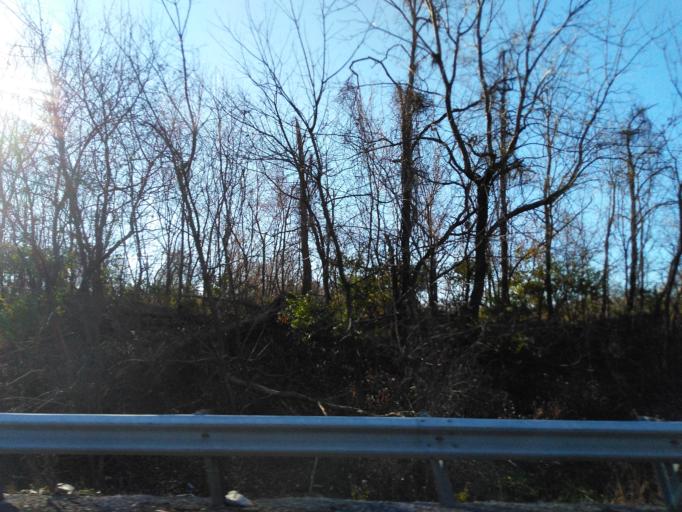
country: US
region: Illinois
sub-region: Madison County
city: Troy
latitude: 38.7555
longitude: -89.8751
